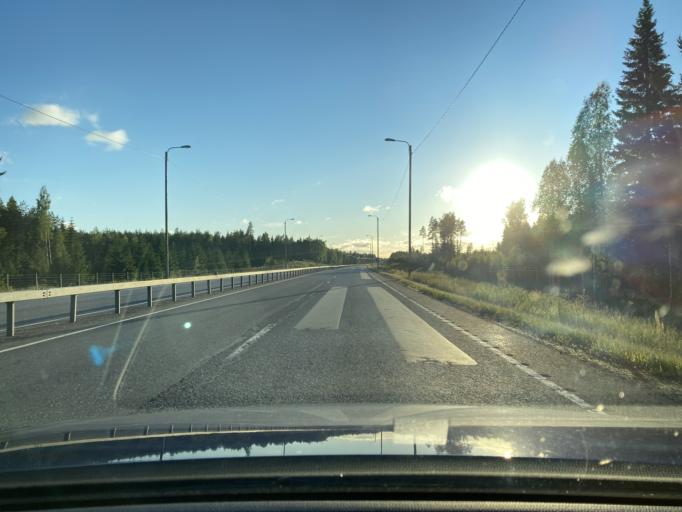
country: FI
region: Uusimaa
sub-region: Helsinki
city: Kaerkoelae
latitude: 60.6321
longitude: 23.9194
